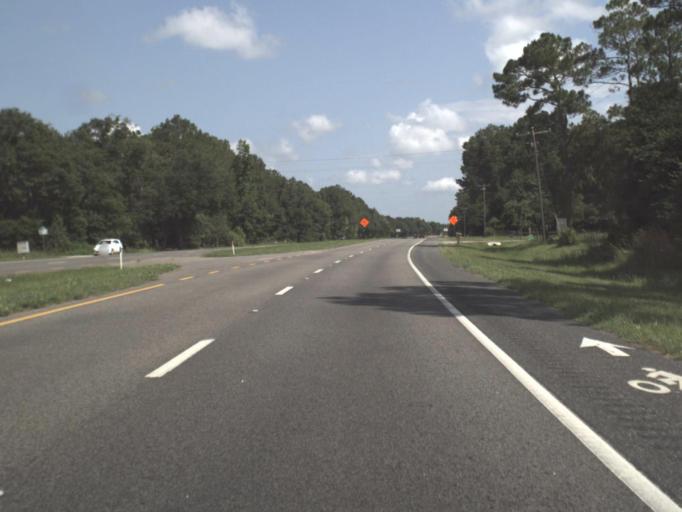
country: US
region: Florida
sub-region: Alachua County
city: Gainesville
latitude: 29.5491
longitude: -82.3253
